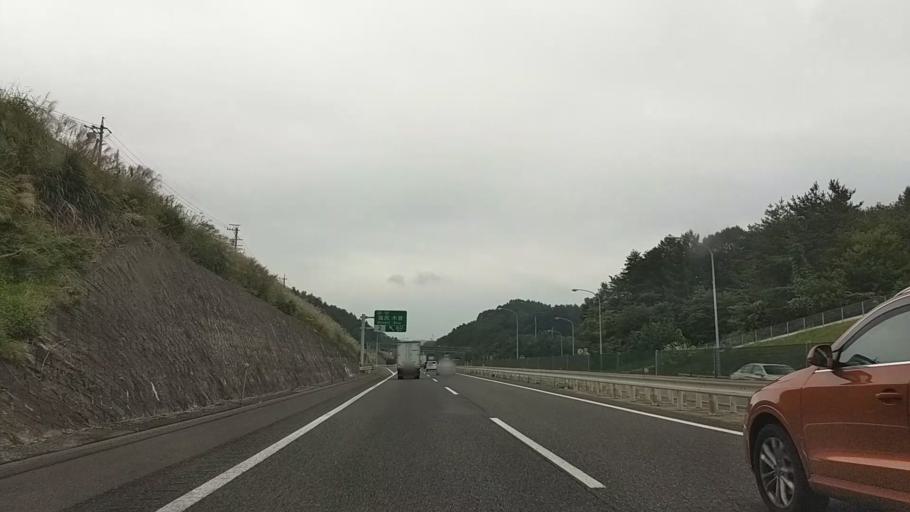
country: JP
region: Nagano
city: Shiojiri
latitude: 36.1206
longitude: 137.9802
